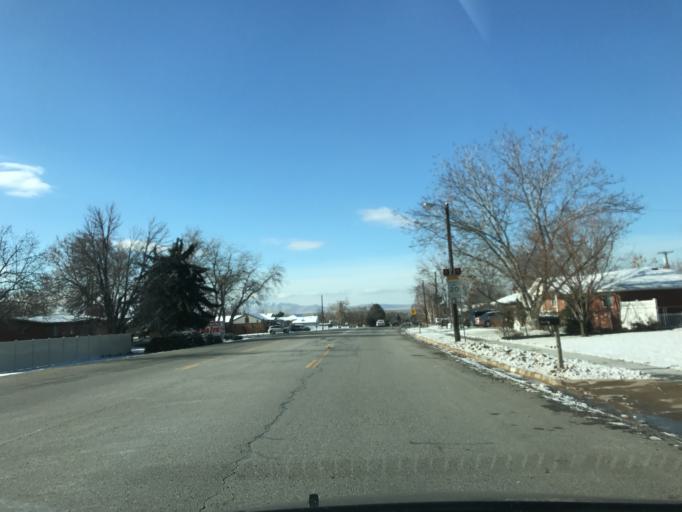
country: US
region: Utah
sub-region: Davis County
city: Kaysville
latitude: 41.0381
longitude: -111.9235
